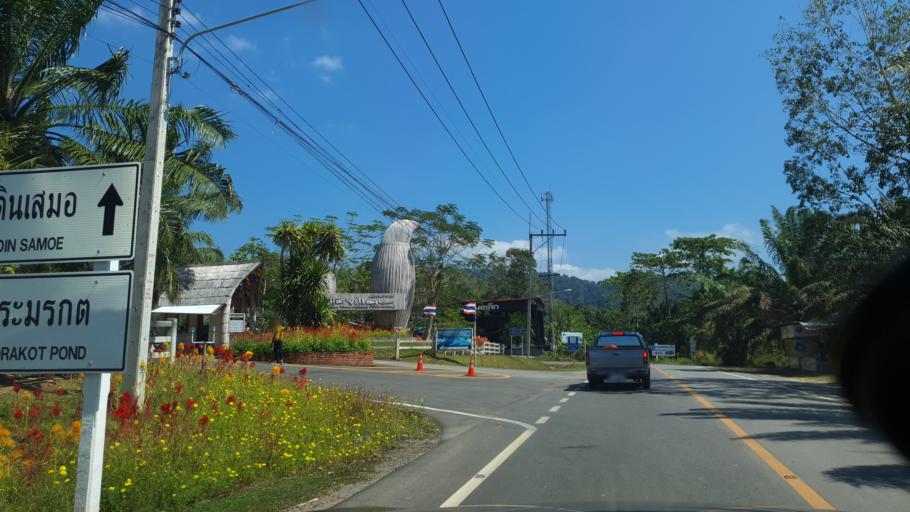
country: TH
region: Krabi
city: Khlong Thom
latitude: 7.9213
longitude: 99.2590
